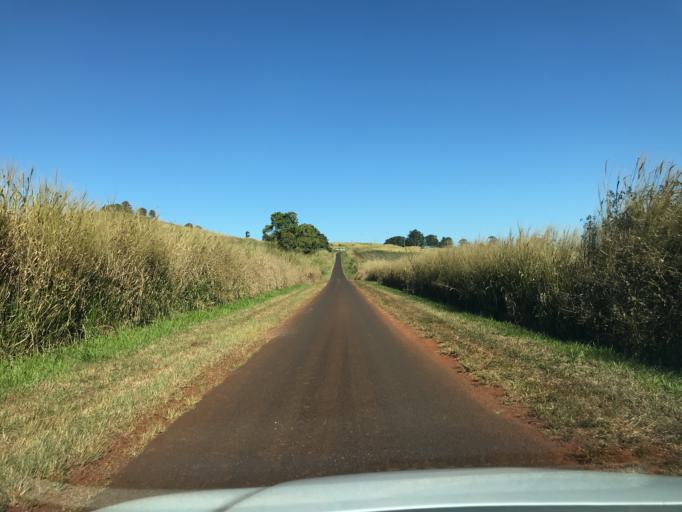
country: AU
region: Queensland
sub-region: Tablelands
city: Atherton
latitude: -17.2878
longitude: 145.5432
